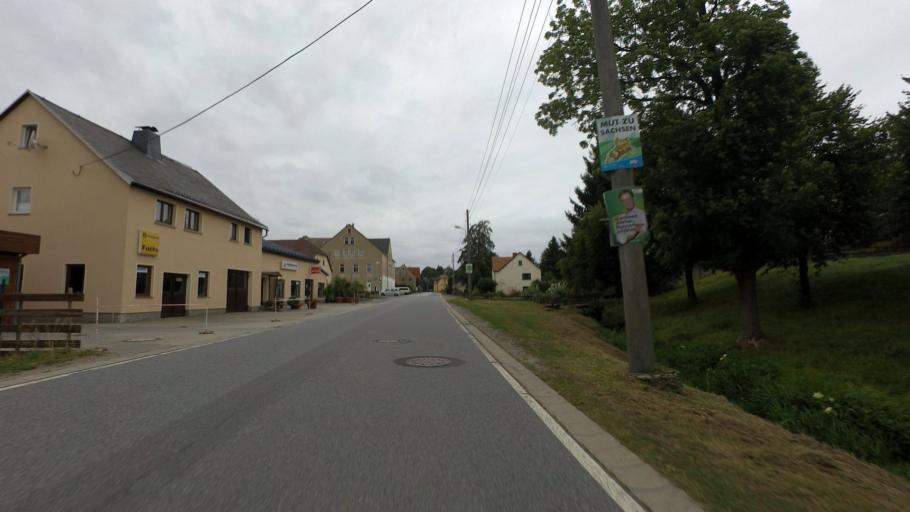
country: DE
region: Saxony
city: Berthelsdorf
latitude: 51.0632
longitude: 14.2187
